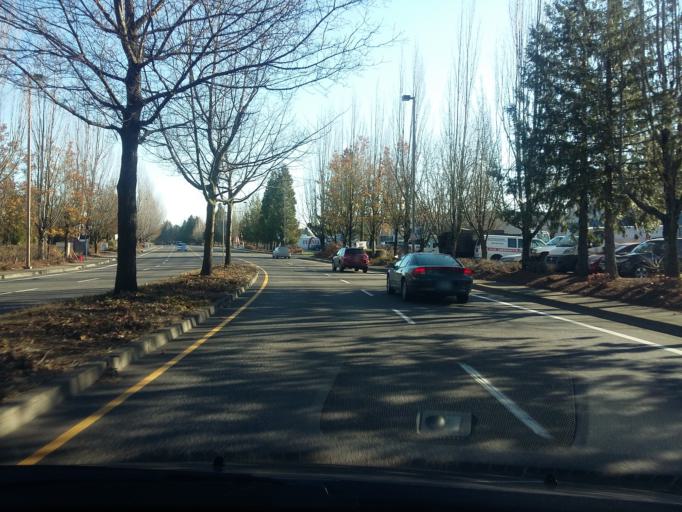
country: US
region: Washington
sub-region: Clark County
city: Mill Plain
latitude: 45.5631
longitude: -122.5289
